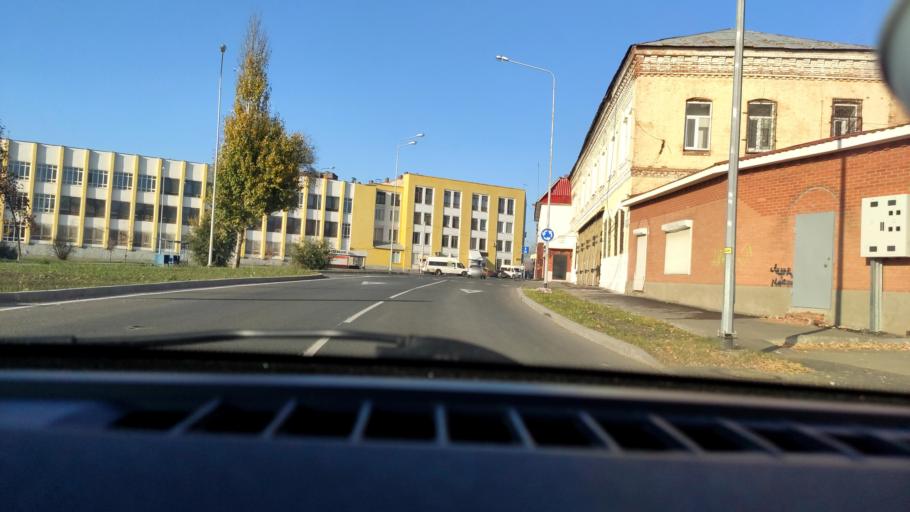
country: RU
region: Samara
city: Rozhdestveno
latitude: 53.1789
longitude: 50.0813
